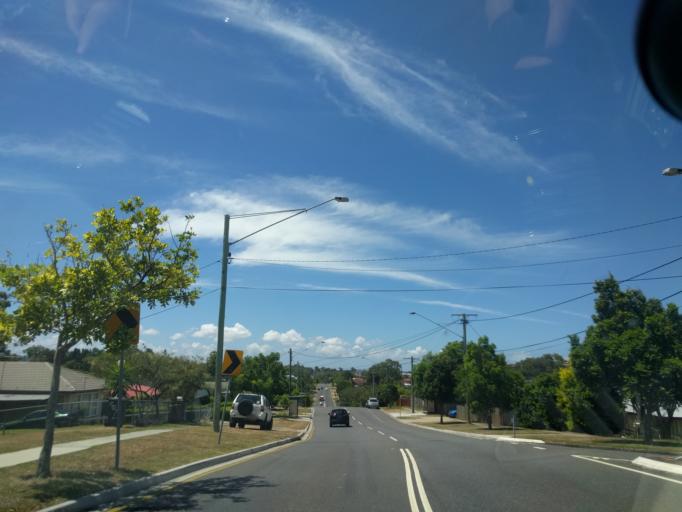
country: AU
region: Queensland
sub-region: Brisbane
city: Stafford Heights
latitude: -27.3989
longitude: 153.0099
